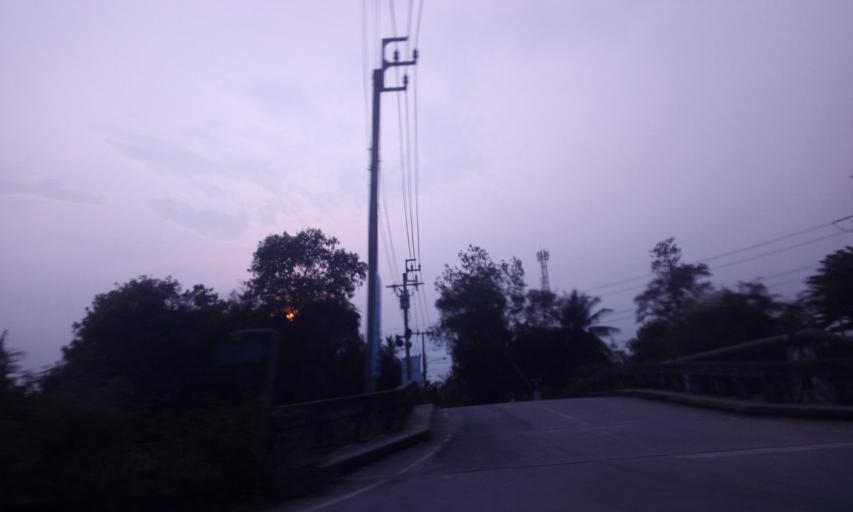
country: TH
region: Bangkok
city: Nong Chok
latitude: 13.9284
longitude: 100.8928
